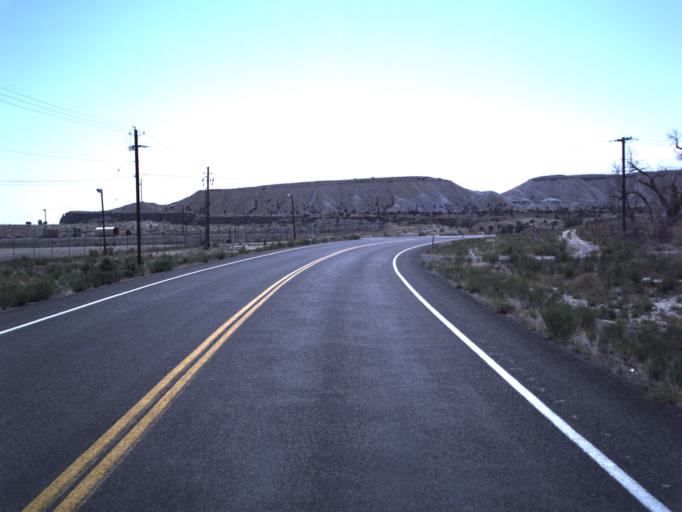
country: US
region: Utah
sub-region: Emery County
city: Orangeville
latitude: 39.2401
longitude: -111.0888
